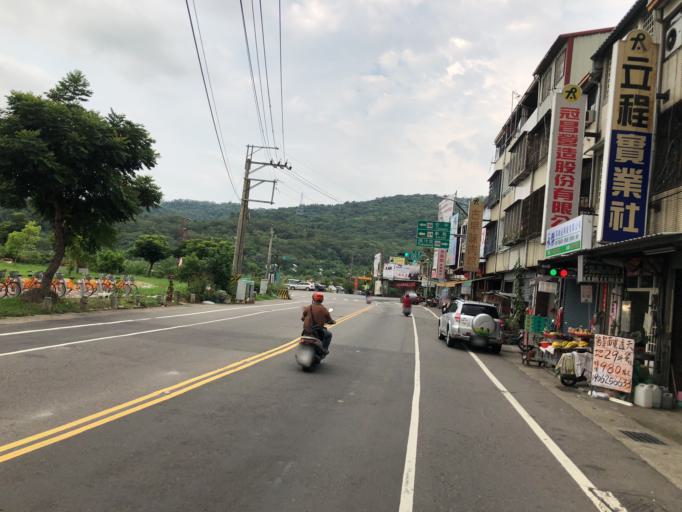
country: TW
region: Taiwan
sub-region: Taichung City
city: Taichung
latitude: 24.1308
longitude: 120.7372
